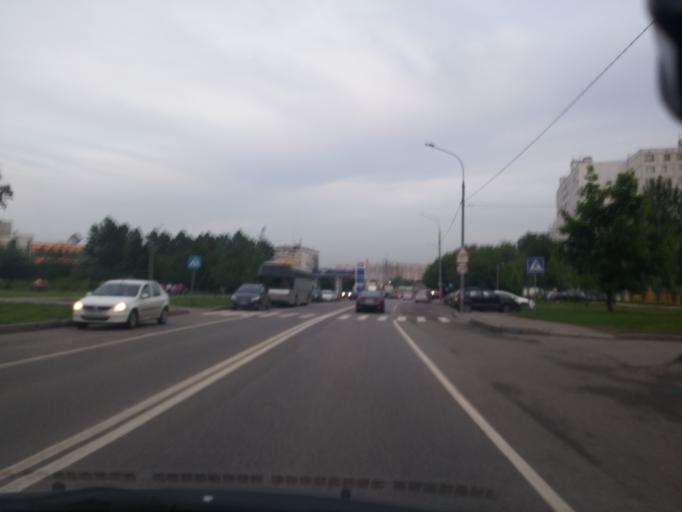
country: RU
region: Moscow
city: Bibirevo
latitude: 55.8858
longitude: 37.5979
